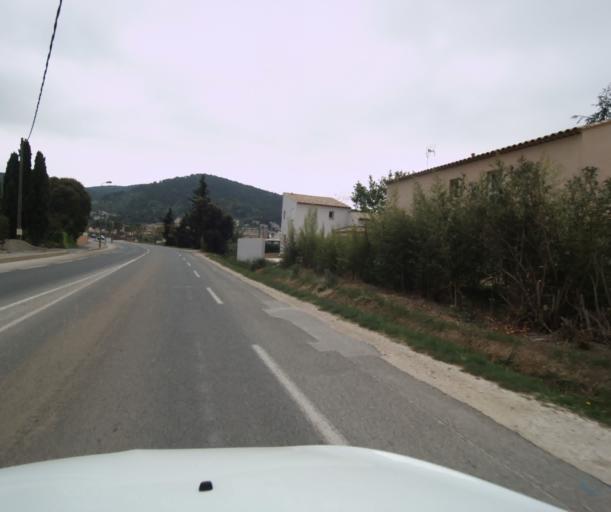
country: FR
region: Provence-Alpes-Cote d'Azur
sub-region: Departement du Var
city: La Crau
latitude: 43.1237
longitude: 6.0732
